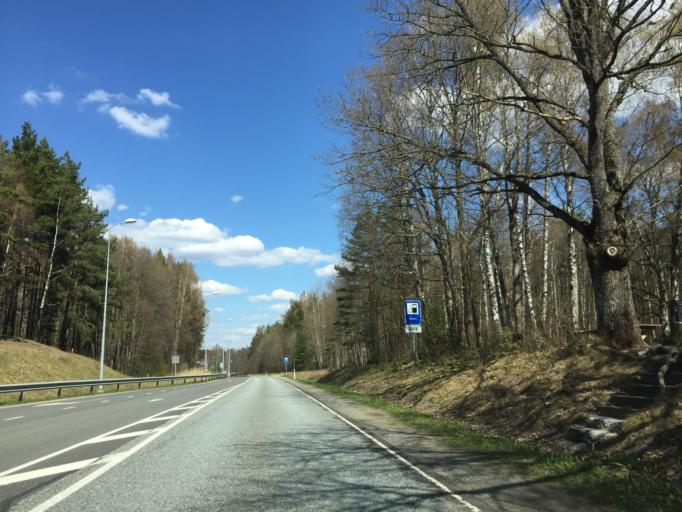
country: LV
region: Saulkrastu
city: Saulkrasti
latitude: 57.2258
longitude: 24.3920
